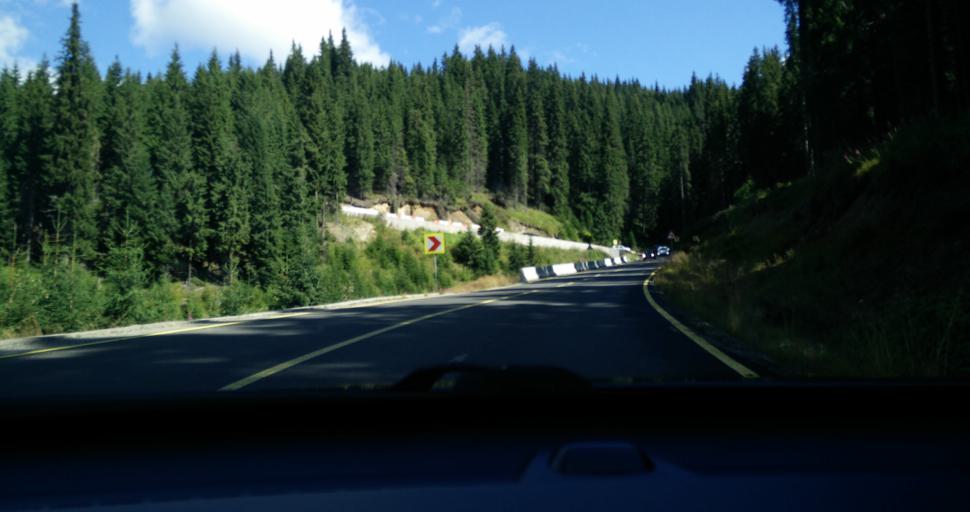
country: RO
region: Hunedoara
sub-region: Oras Petrila
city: Petrila
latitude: 45.4495
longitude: 23.6196
